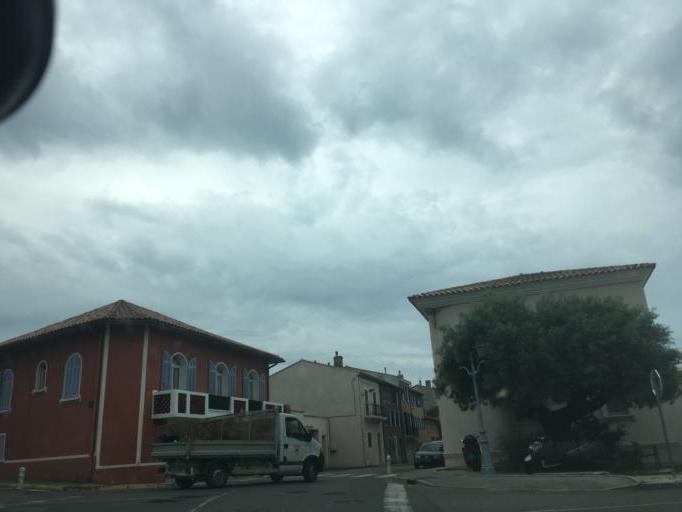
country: FR
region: Provence-Alpes-Cote d'Azur
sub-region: Departement du Var
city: La Londe-les-Maures
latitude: 43.1405
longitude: 6.2320
